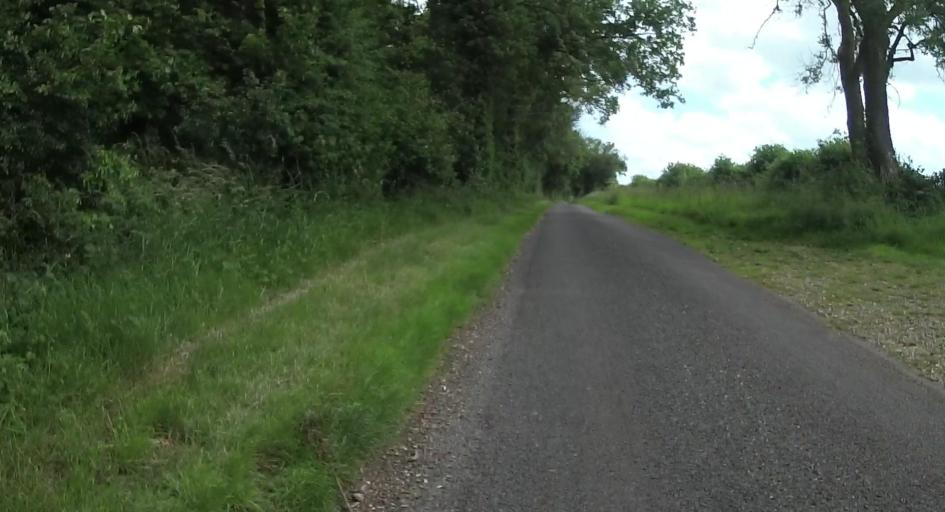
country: GB
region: England
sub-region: Hampshire
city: Four Marks
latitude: 51.1516
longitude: -1.1552
